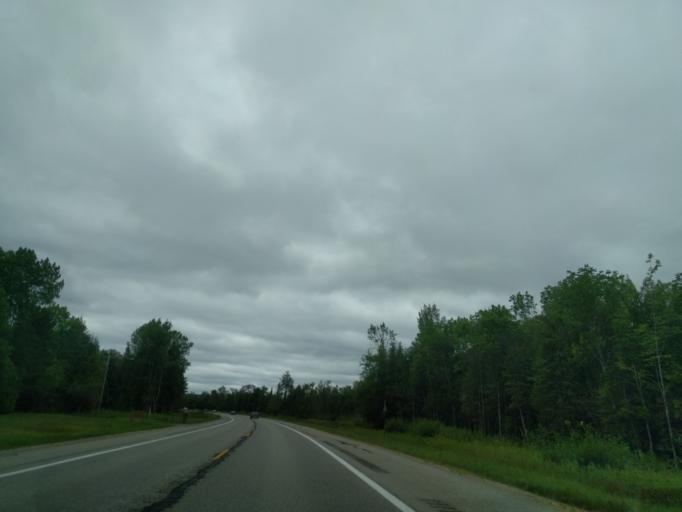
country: US
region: Michigan
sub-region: Delta County
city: Escanaba
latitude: 45.6642
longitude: -87.1707
